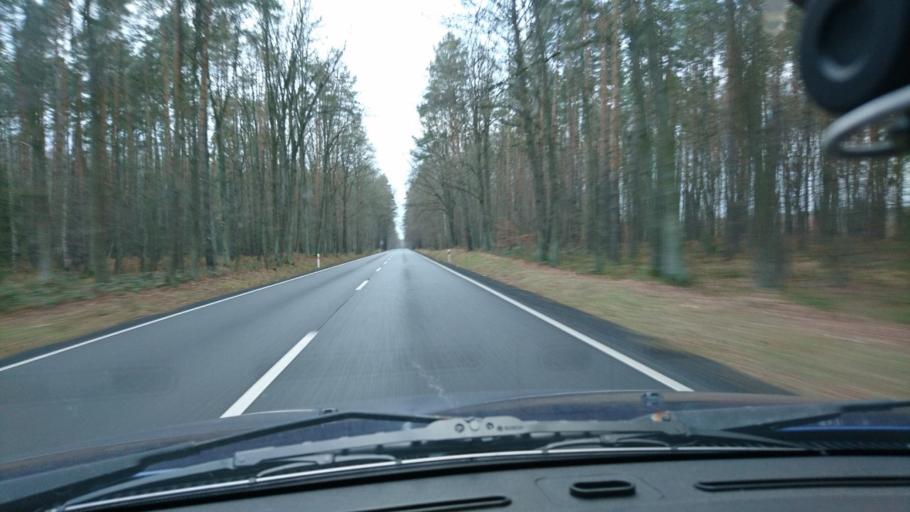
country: PL
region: Opole Voivodeship
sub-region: Powiat oleski
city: Olesno
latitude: 50.9250
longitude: 18.3370
